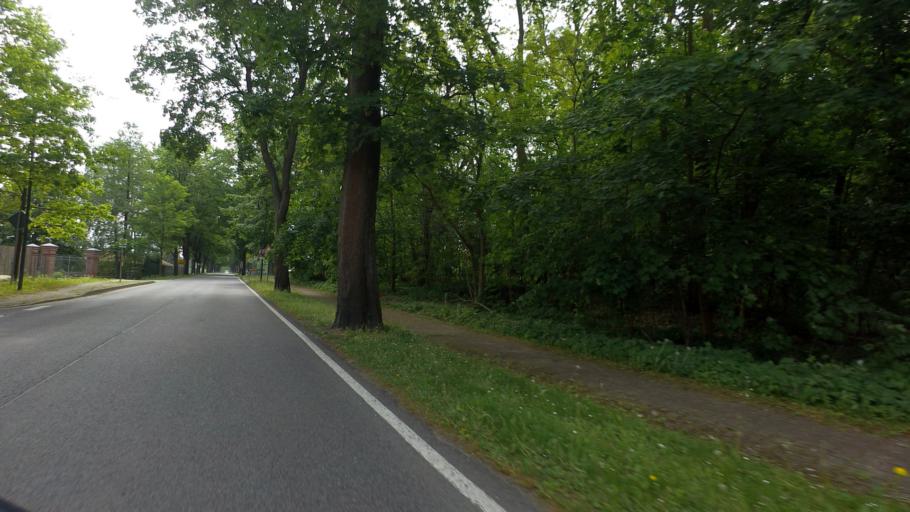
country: DE
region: Brandenburg
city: Lieberose
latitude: 51.9752
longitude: 14.3024
